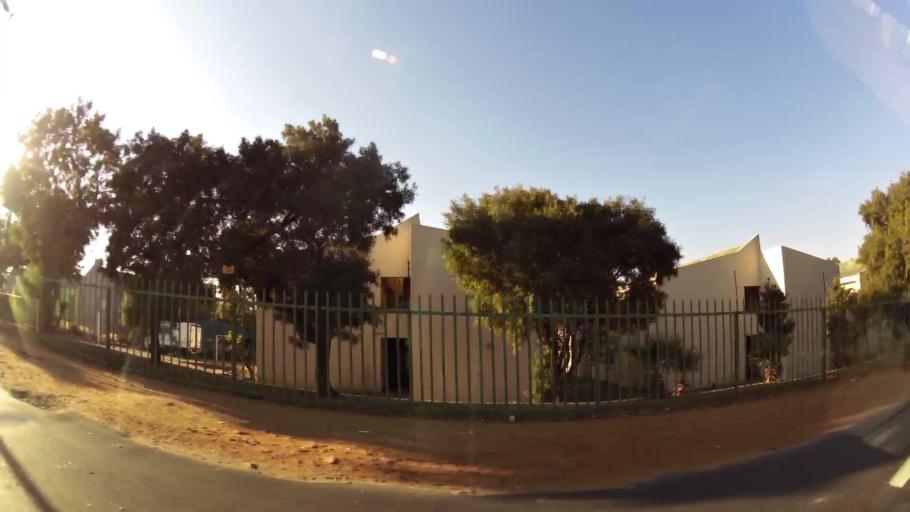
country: ZA
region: Gauteng
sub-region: City of Johannesburg Metropolitan Municipality
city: Midrand
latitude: -26.0222
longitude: 28.1323
